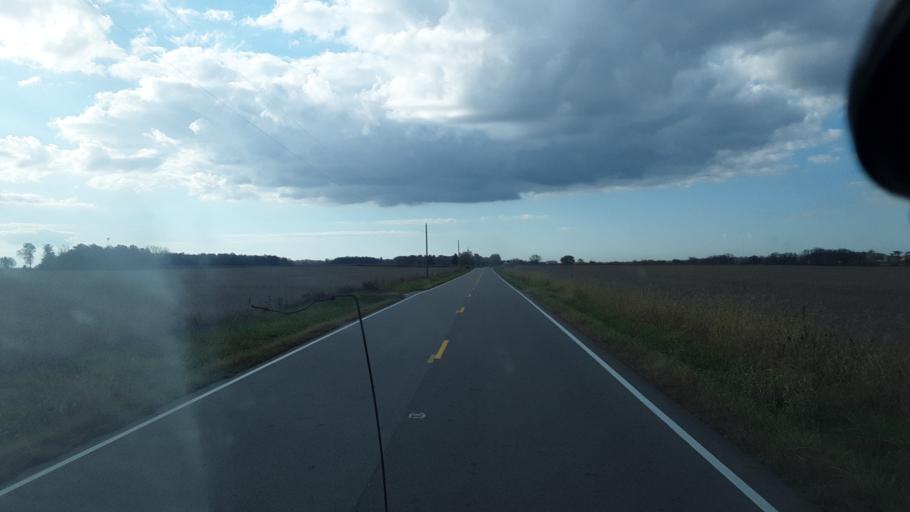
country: US
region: Ohio
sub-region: Highland County
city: Greenfield
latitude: 39.4327
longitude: -83.4406
